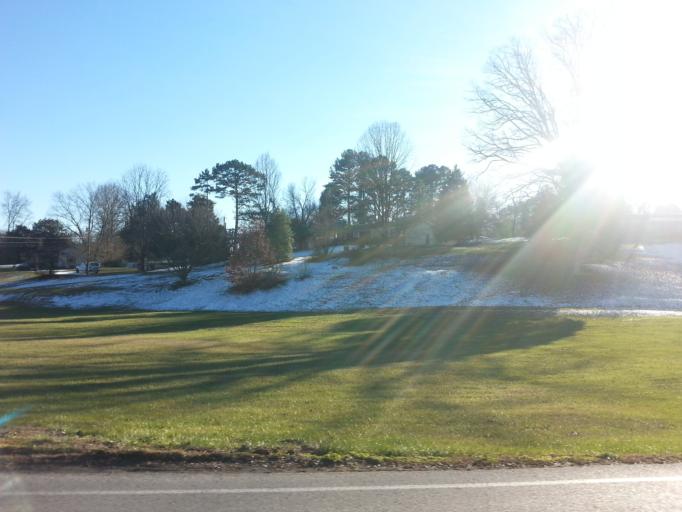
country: US
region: Tennessee
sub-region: Knox County
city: Farragut
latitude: 35.9574
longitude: -84.0502
